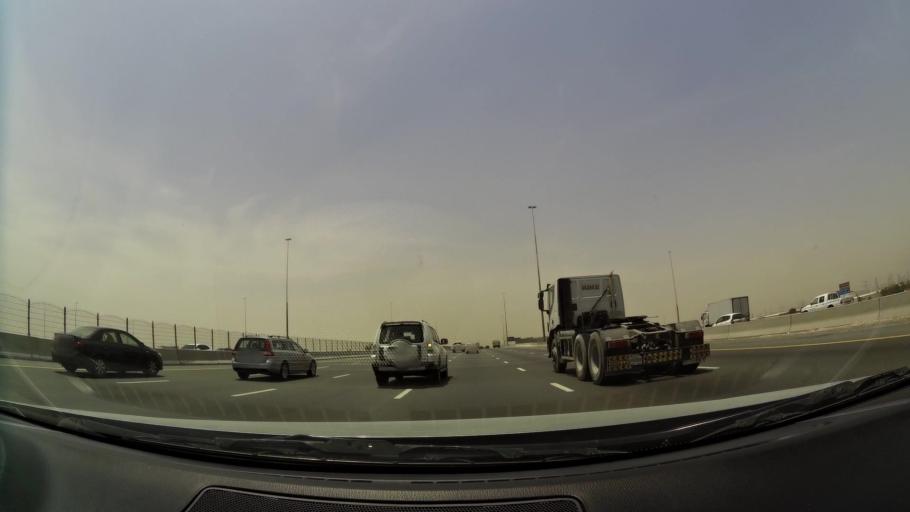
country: AE
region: Ash Shariqah
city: Sharjah
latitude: 25.1829
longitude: 55.3966
